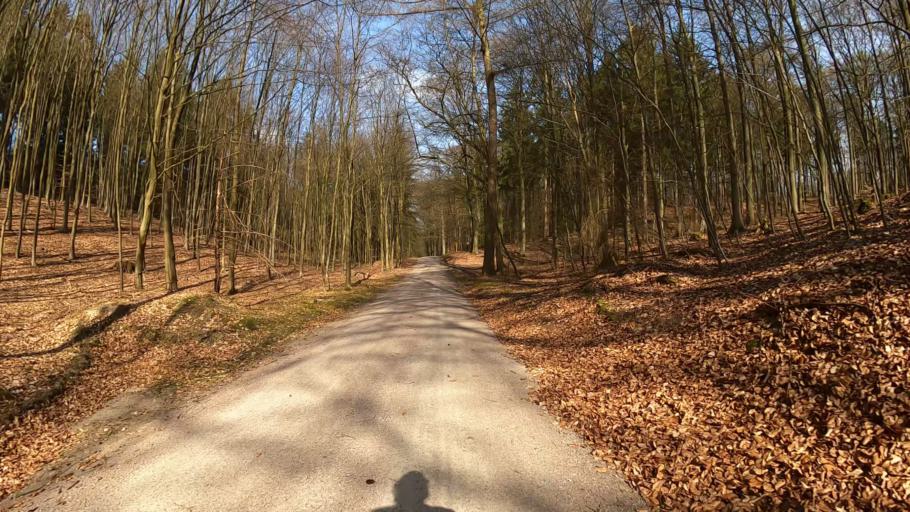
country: DE
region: Hamburg
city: Harburg
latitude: 53.4617
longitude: 9.9125
